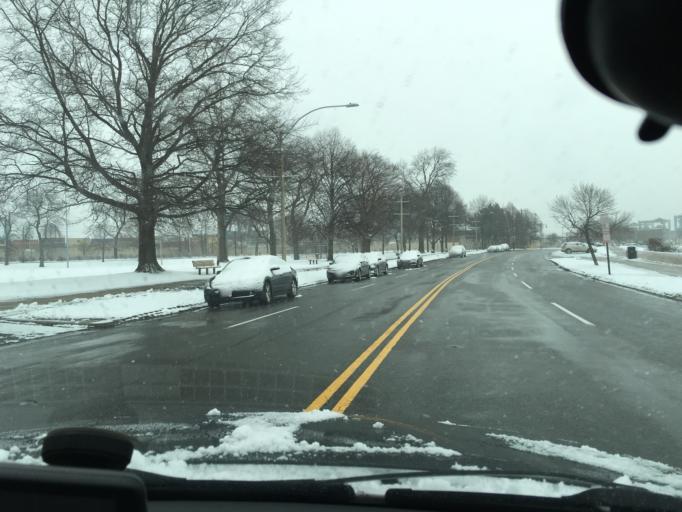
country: US
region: Massachusetts
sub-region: Suffolk County
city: South Boston
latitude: 42.3369
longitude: -71.0232
